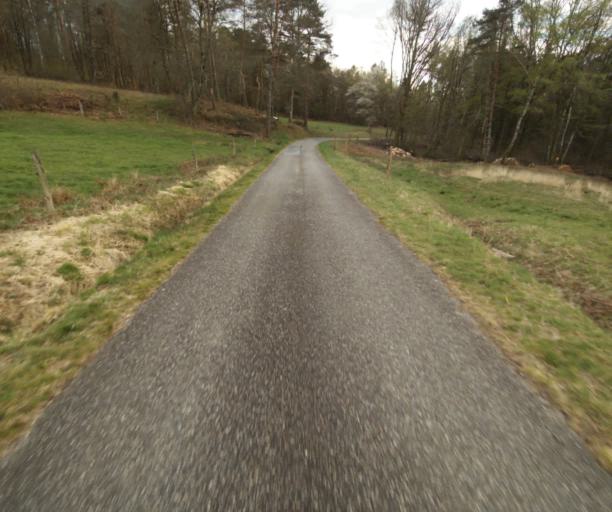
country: FR
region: Limousin
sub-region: Departement de la Correze
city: Argentat
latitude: 45.2007
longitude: 1.9879
